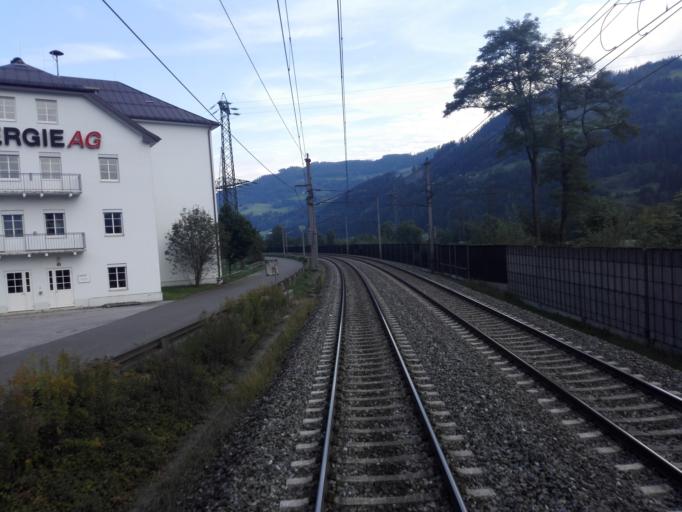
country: AT
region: Salzburg
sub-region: Politischer Bezirk Sankt Johann im Pongau
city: Sankt Johann im Pongau
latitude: 47.3775
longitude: 13.2106
